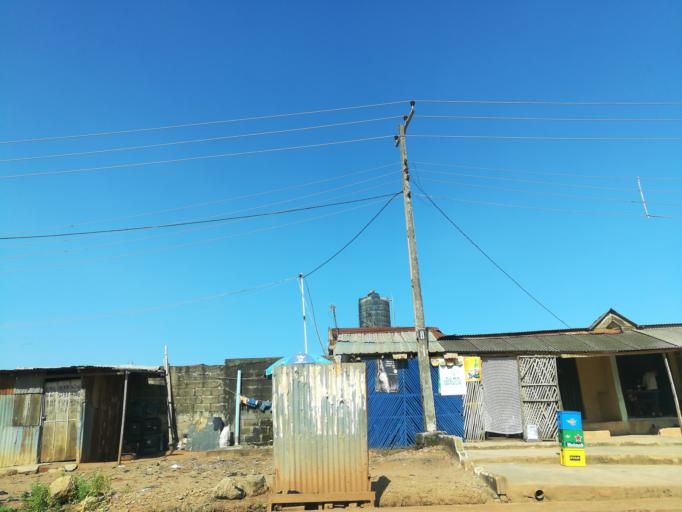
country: NG
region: Lagos
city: Ikorodu
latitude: 6.5834
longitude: 3.5222
